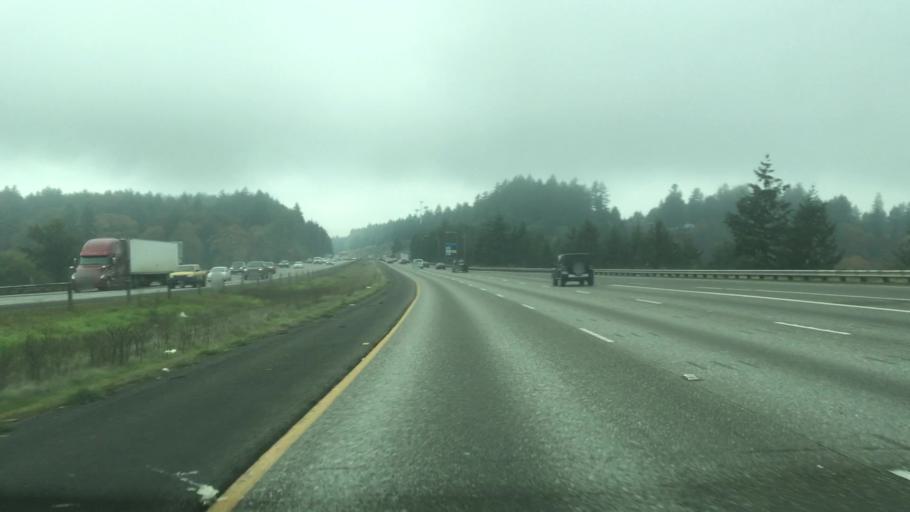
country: US
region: Washington
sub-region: Thurston County
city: Tanglewilde-Thompson Place
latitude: 47.0682
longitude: -122.7247
